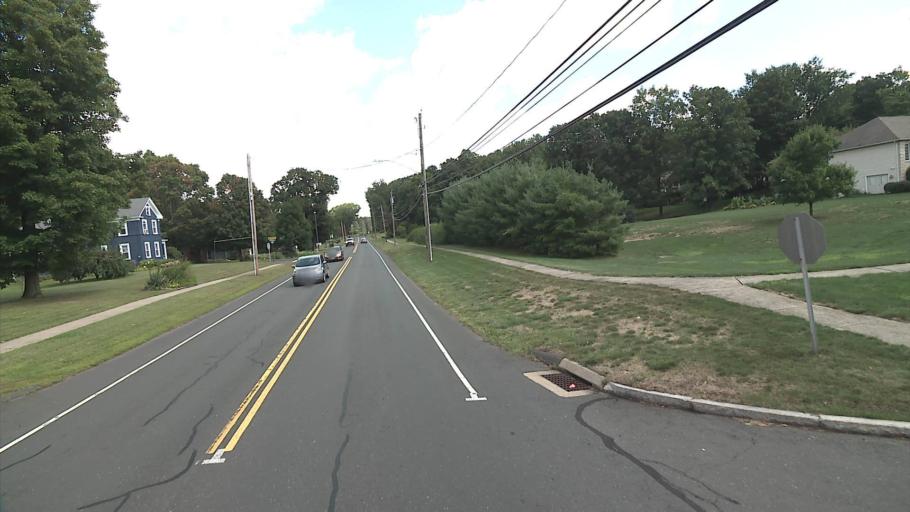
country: US
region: Connecticut
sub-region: Hartford County
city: Newington
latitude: 41.6489
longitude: -72.7114
